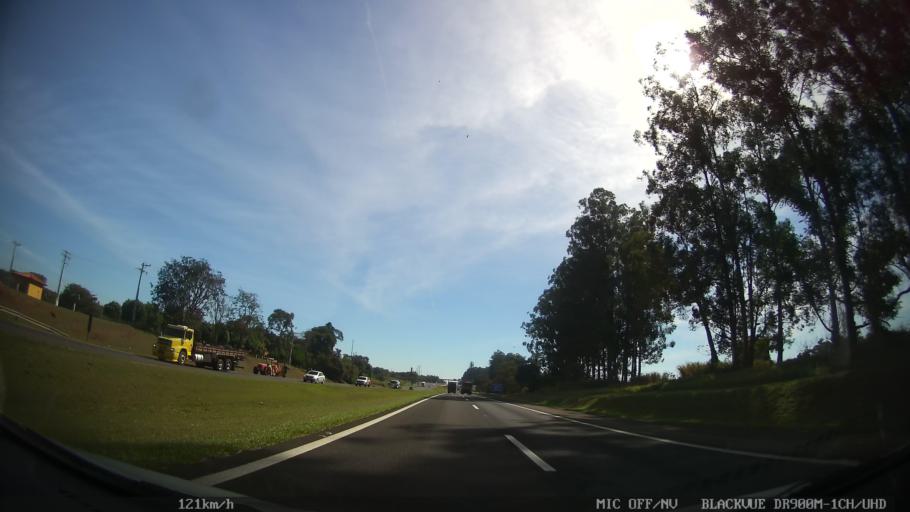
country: BR
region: Sao Paulo
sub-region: Pirassununga
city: Pirassununga
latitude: -21.9639
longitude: -47.4574
